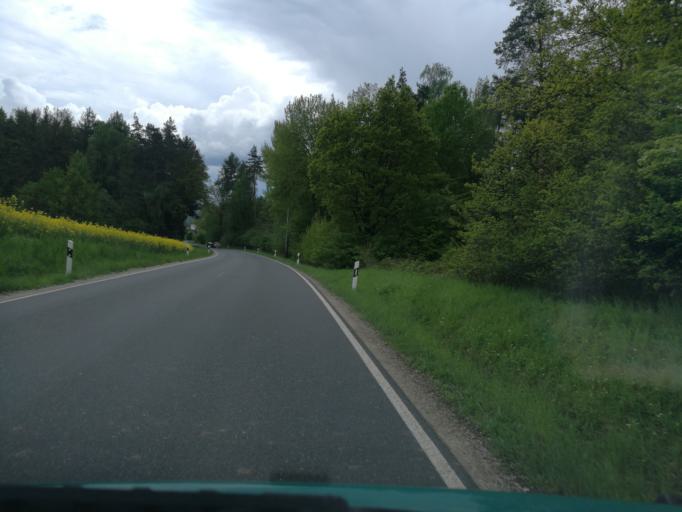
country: DE
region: Bavaria
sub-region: Upper Franconia
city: Michelau
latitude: 50.1864
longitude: 11.1177
